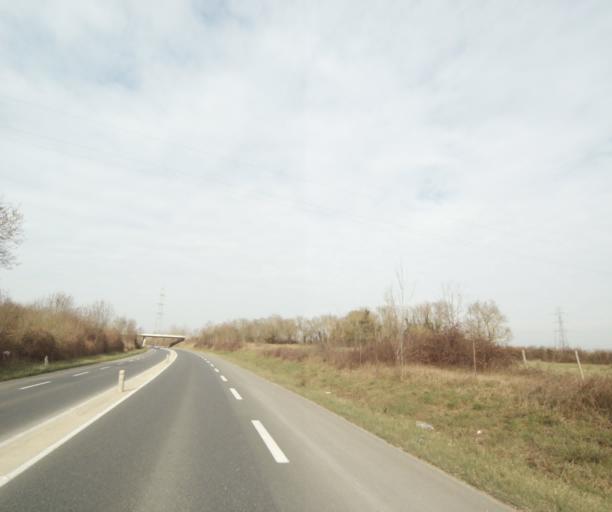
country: FR
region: Poitou-Charentes
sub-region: Departement des Deux-Sevres
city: Niort
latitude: 46.2992
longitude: -0.4760
